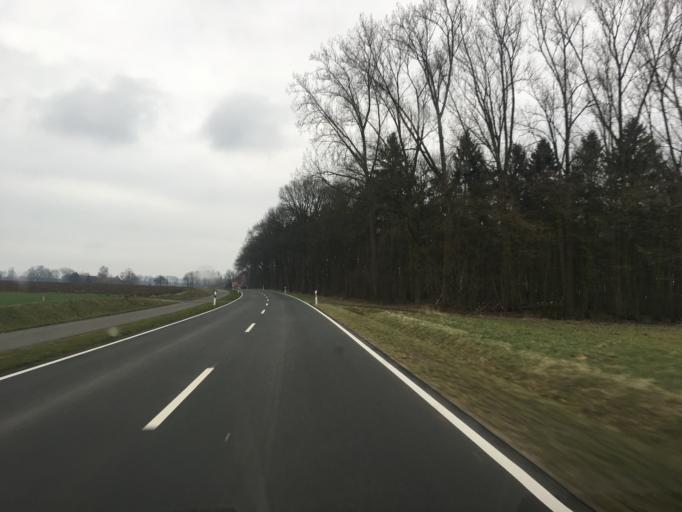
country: DE
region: North Rhine-Westphalia
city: Olfen
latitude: 51.7257
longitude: 7.4021
